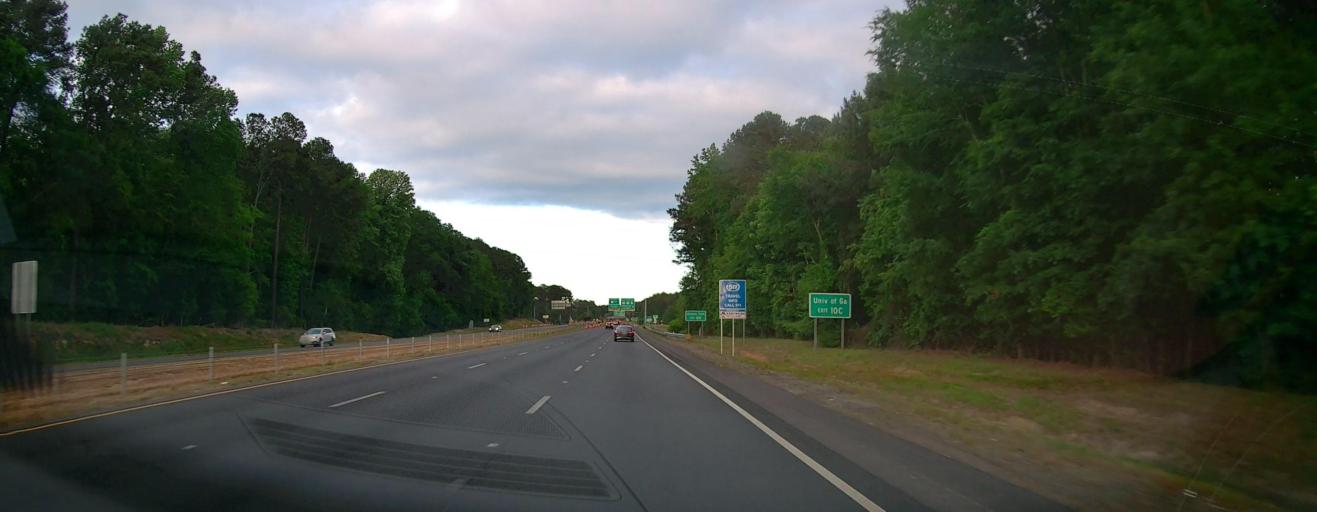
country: US
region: Georgia
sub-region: Clarke County
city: Athens
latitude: 33.9782
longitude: -83.3596
